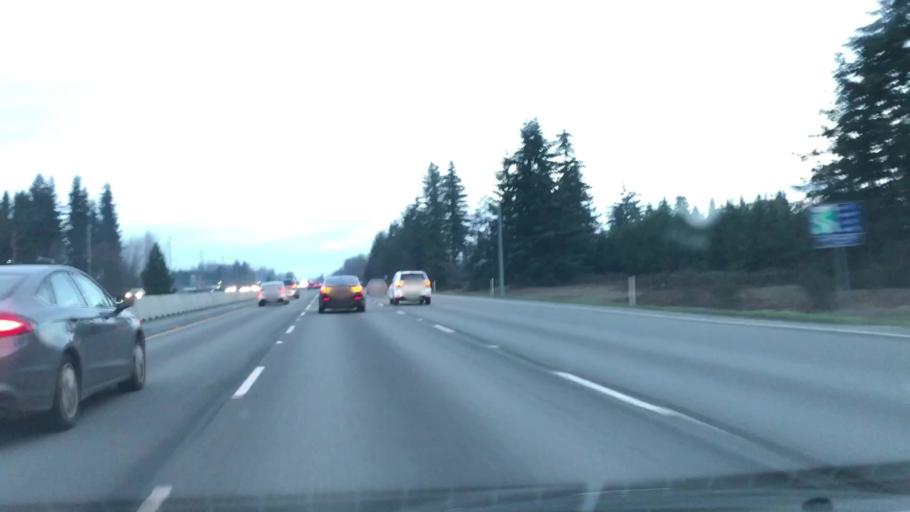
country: US
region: Washington
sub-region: Snohomish County
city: Smokey Point
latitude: 48.1050
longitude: -122.1842
